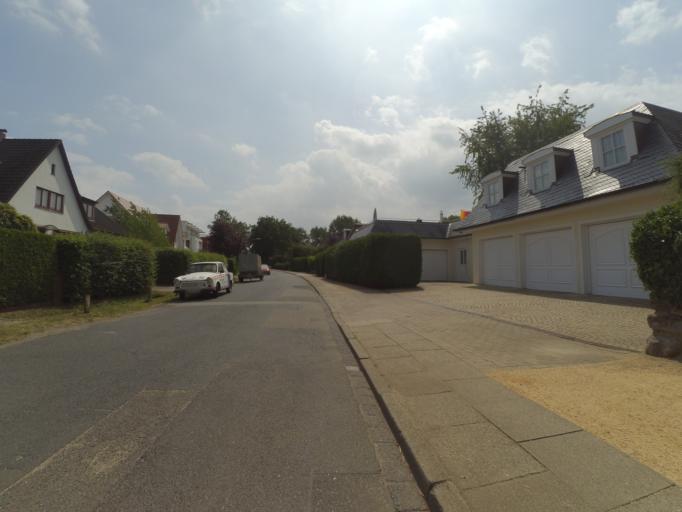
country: DE
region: Schleswig-Holstein
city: Bonningstedt
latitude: 53.6331
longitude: 9.9365
